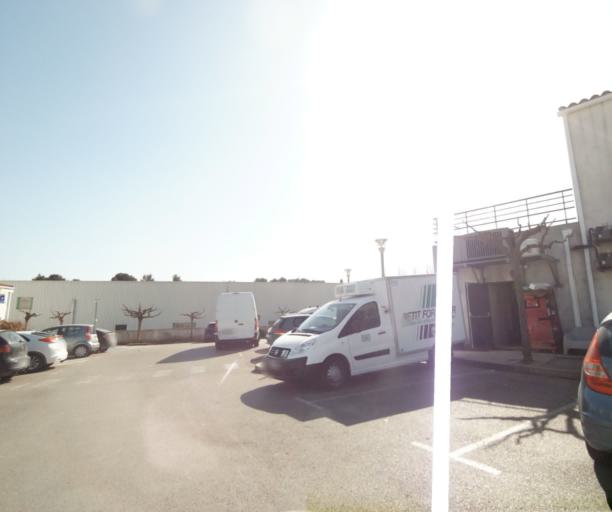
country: FR
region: Provence-Alpes-Cote d'Azur
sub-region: Departement des Bouches-du-Rhone
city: Gardanne
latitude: 43.4539
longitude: 5.4527
